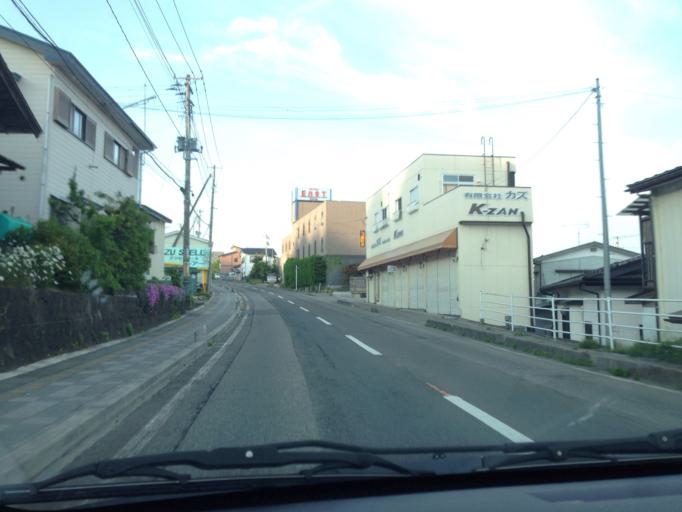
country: JP
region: Fukushima
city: Kitakata
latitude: 37.4968
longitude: 139.9497
